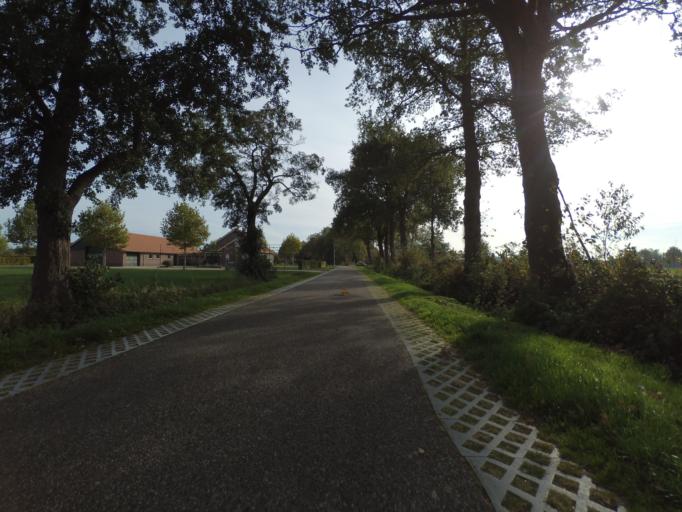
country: NL
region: Overijssel
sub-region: Gemeente Raalte
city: Raalte
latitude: 52.3594
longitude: 6.3691
